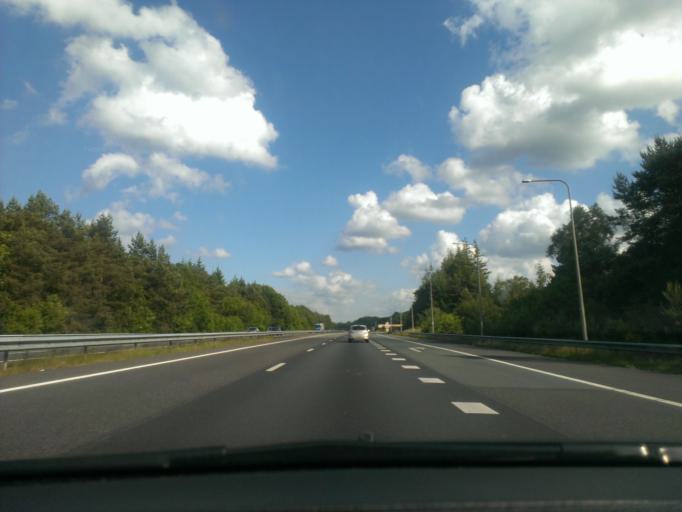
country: NL
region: Gelderland
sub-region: Gemeente Apeldoorn
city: Uddel
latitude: 52.1990
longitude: 5.8301
